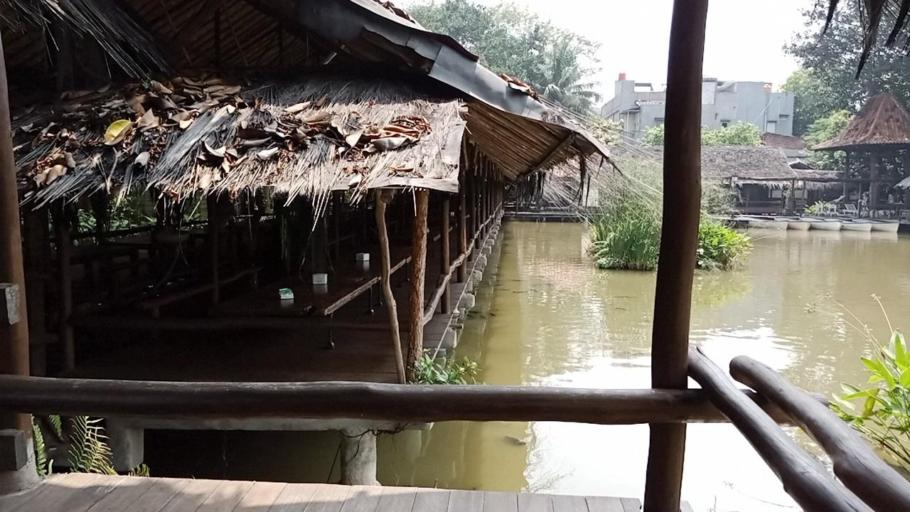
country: ID
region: West Java
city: Sawangan
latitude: -6.3950
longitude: 106.7886
